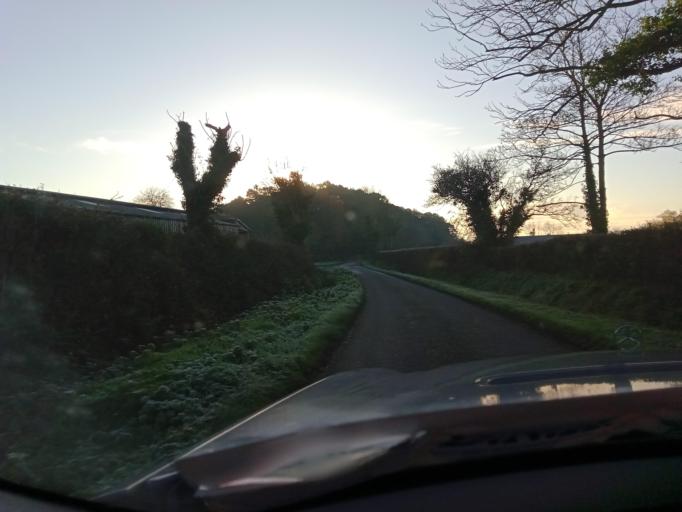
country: IE
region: Leinster
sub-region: Kilkenny
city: Callan
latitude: 52.5351
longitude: -7.4299
